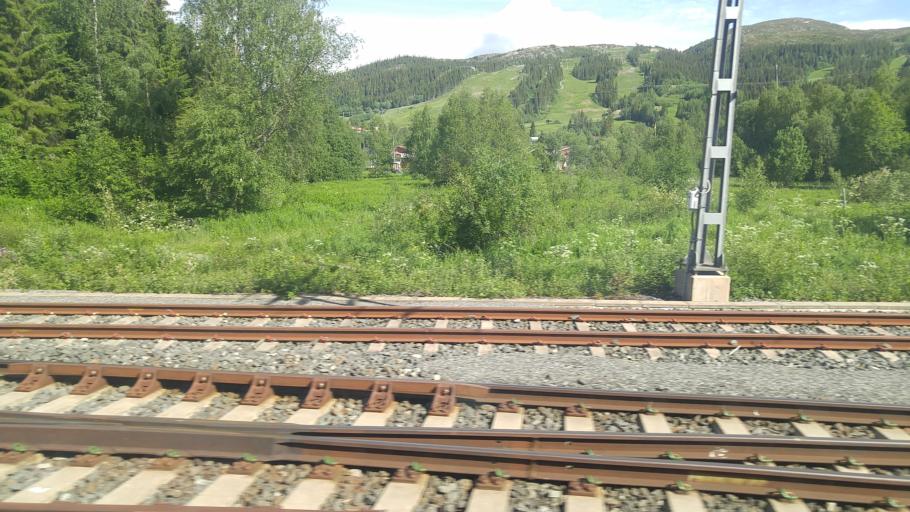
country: SE
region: Jaemtland
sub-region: Are Kommun
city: Are
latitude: 63.3900
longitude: 12.9271
